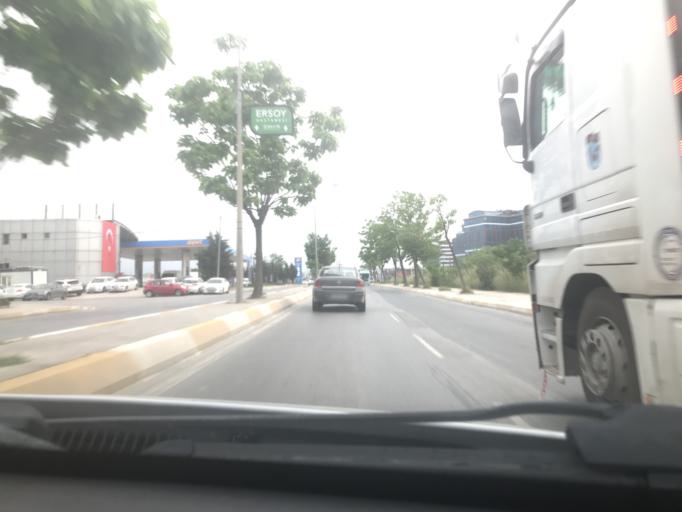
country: TR
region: Istanbul
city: Sultanbeyli
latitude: 40.9274
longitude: 29.3189
